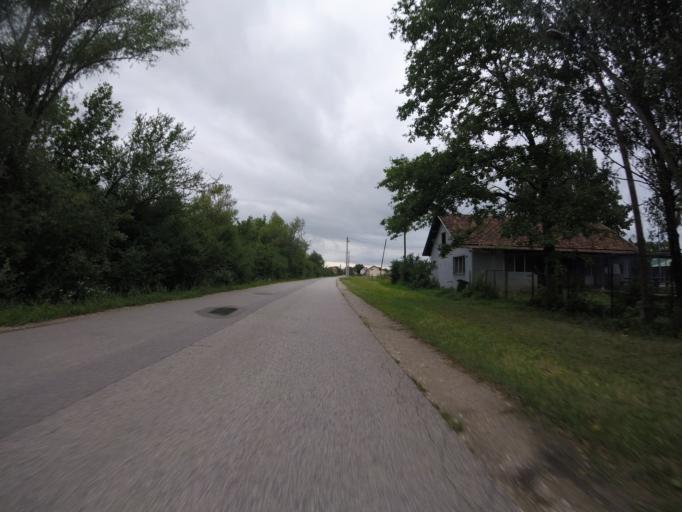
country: HR
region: Zagrebacka
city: Mraclin
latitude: 45.6614
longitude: 16.0990
